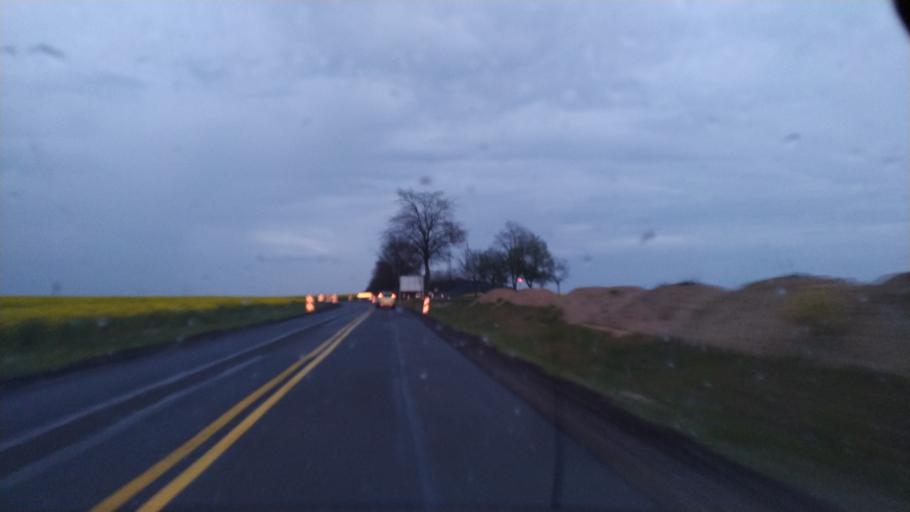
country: PL
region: Greater Poland Voivodeship
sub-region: Powiat pilski
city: Szydlowo
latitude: 53.2435
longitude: 16.6171
